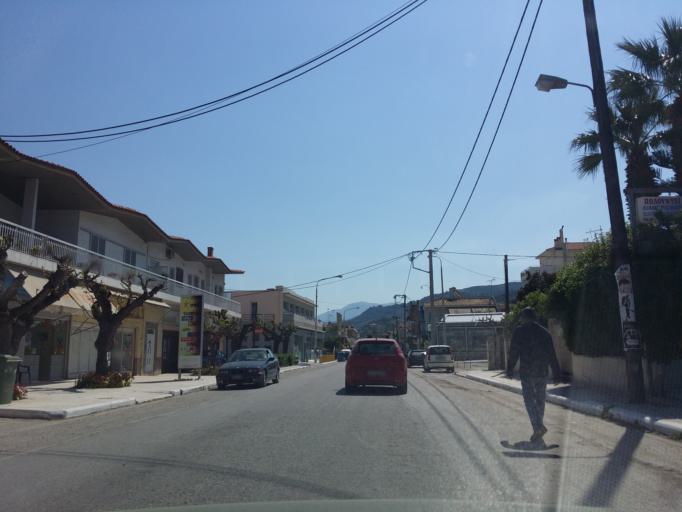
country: GR
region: West Greece
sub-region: Nomos Achaias
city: Aiyira
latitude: 38.1497
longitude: 22.3525
